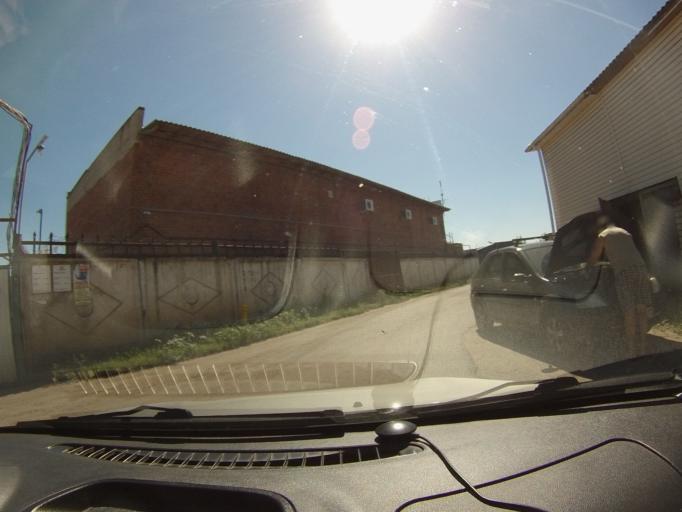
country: RU
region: Tambov
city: Donskoye
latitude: 52.7606
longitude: 41.4659
